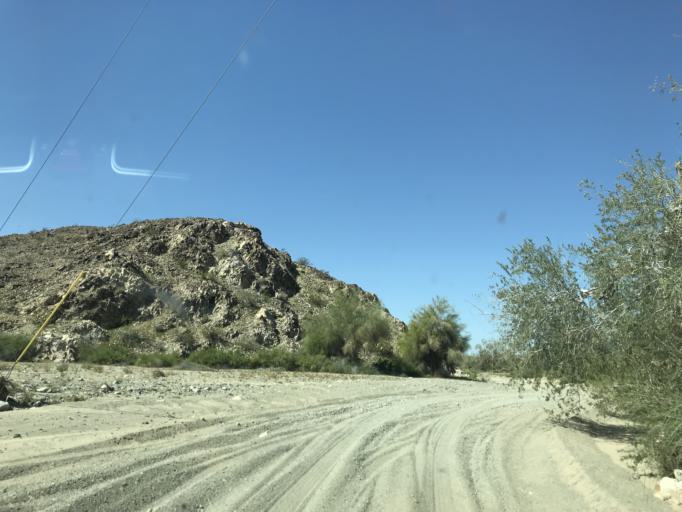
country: US
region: California
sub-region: Riverside County
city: Mesa Verde
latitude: 33.4909
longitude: -114.7928
